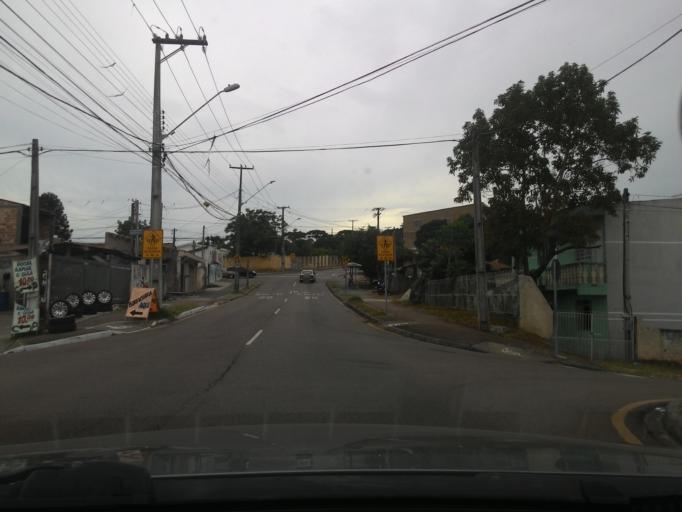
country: BR
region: Parana
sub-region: Pinhais
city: Pinhais
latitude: -25.4470
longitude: -49.2253
